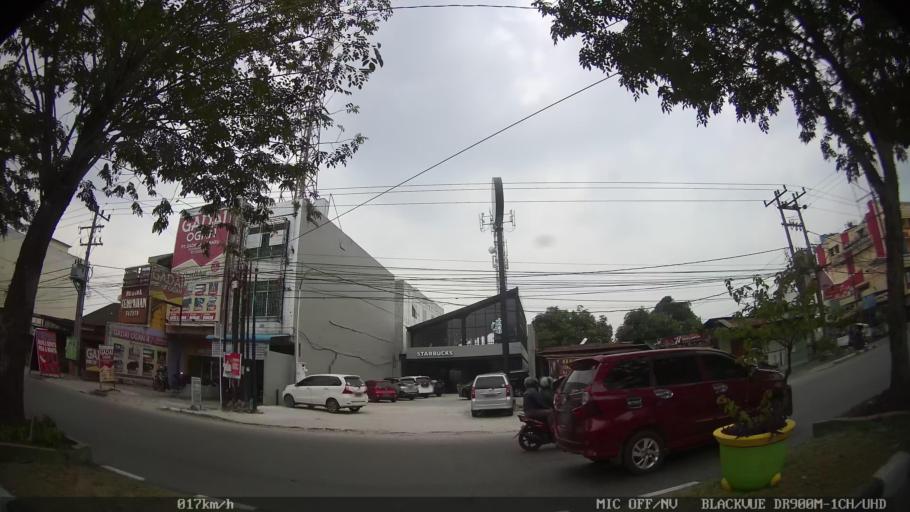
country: ID
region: North Sumatra
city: Medan
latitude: 3.5571
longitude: 98.6947
